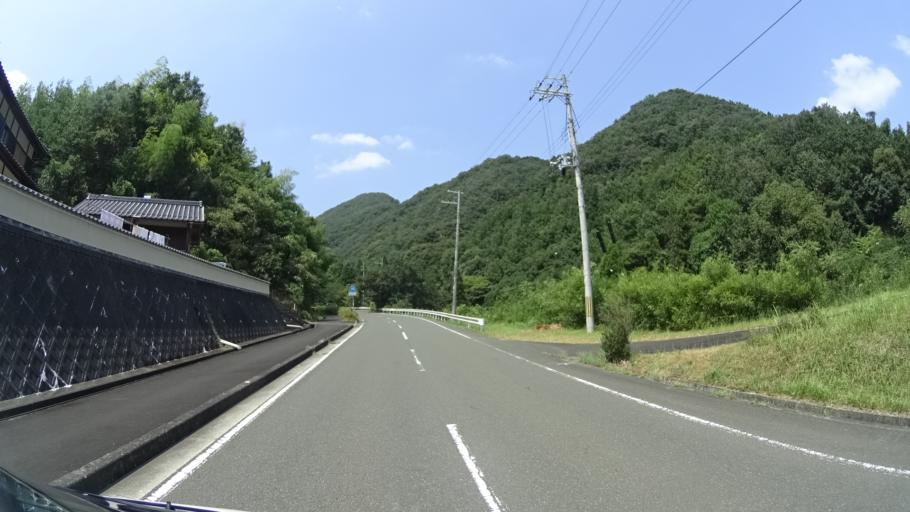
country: JP
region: Kyoto
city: Ayabe
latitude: 35.2241
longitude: 135.2240
